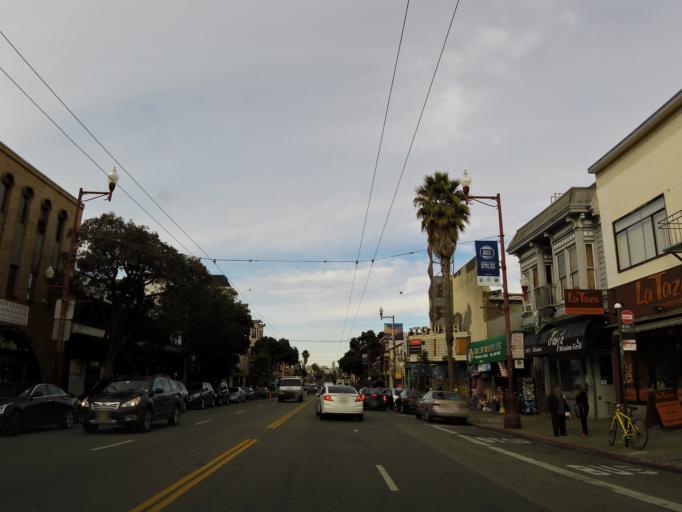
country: US
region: California
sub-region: San Francisco County
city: San Francisco
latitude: 37.7573
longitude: -122.4190
